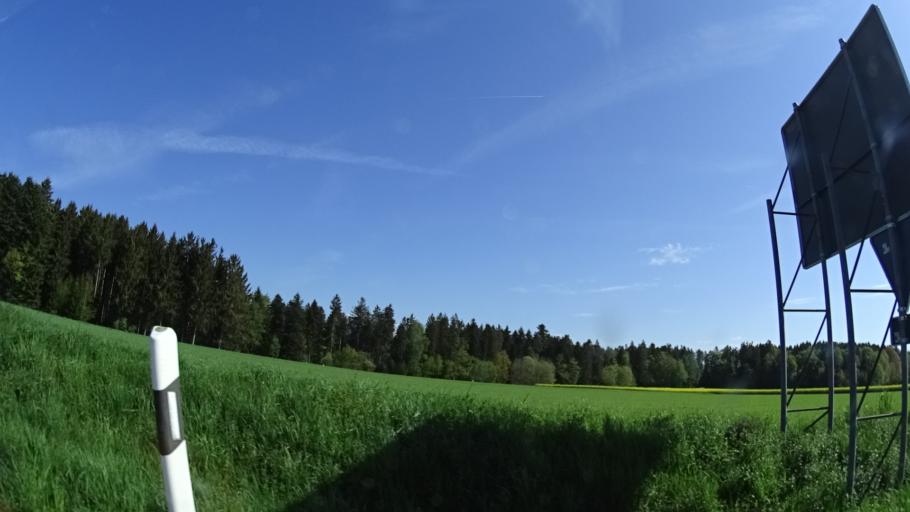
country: DE
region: Baden-Wuerttemberg
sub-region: Karlsruhe Region
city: Neuweiler
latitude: 48.6365
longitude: 8.6081
